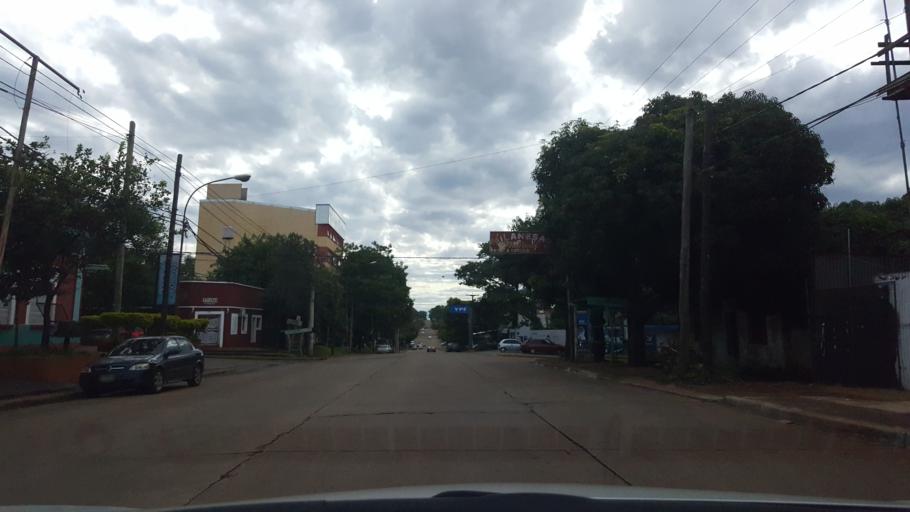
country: AR
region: Misiones
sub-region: Departamento de Capital
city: Posadas
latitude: -27.3729
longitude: -55.9111
